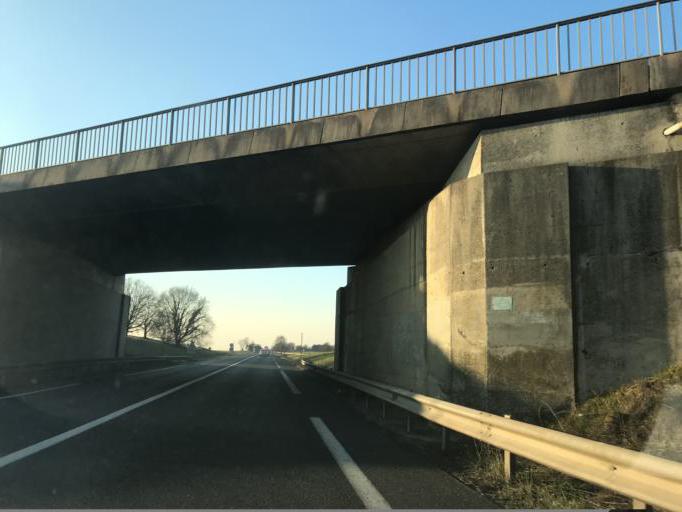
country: FR
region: Ile-de-France
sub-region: Departement de Seine-et-Marne
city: Villiers-sur-Morin
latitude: 48.8555
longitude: 2.8570
